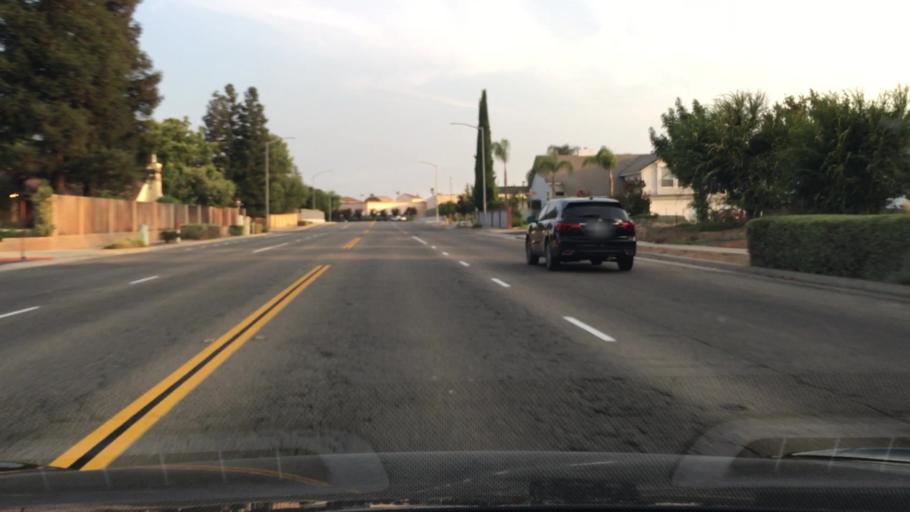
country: US
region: California
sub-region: Fresno County
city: Clovis
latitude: 36.8427
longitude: -119.6930
